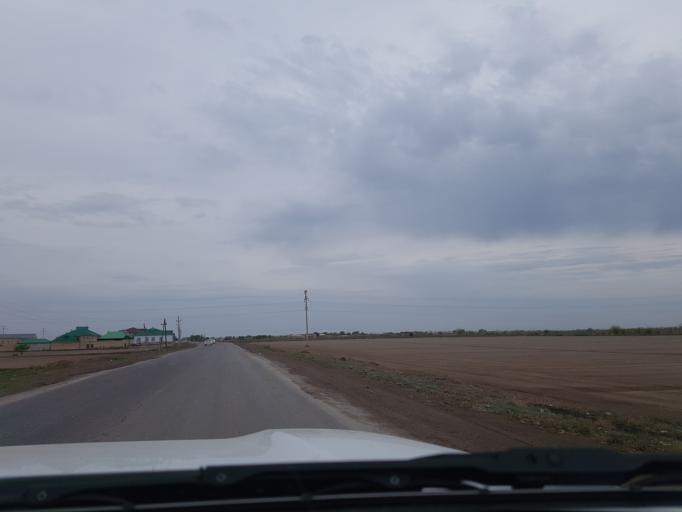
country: TM
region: Lebap
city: Turkmenabat
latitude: 39.0660
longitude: 63.5596
